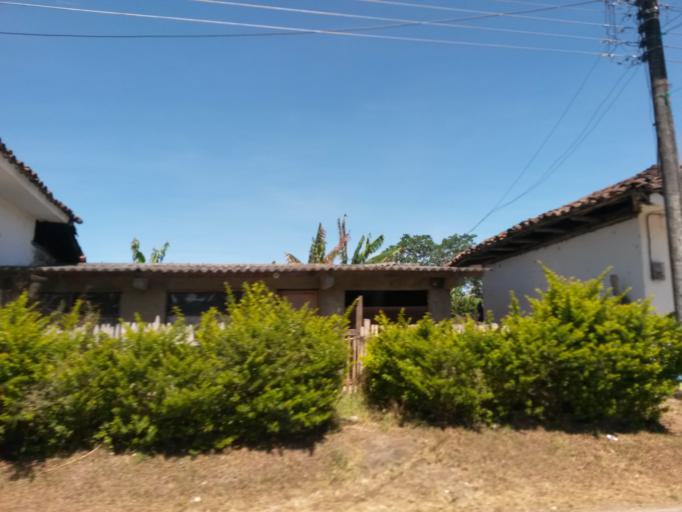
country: CO
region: Cauca
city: Lopez
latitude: 2.4400
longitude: -76.7767
